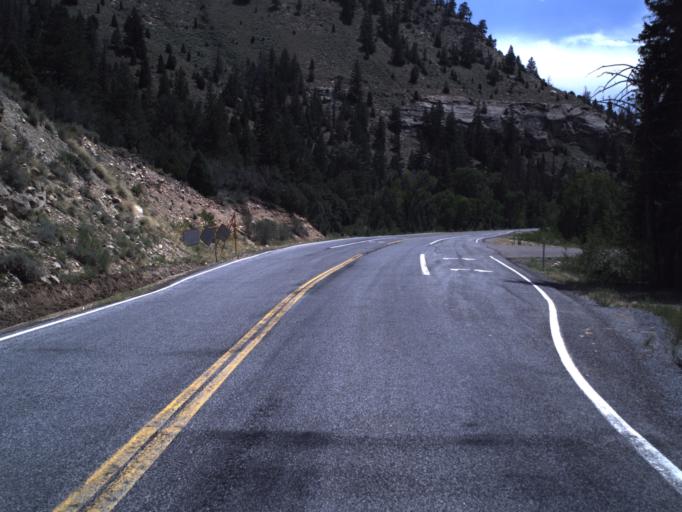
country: US
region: Utah
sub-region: Emery County
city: Huntington
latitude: 39.4635
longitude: -111.1454
